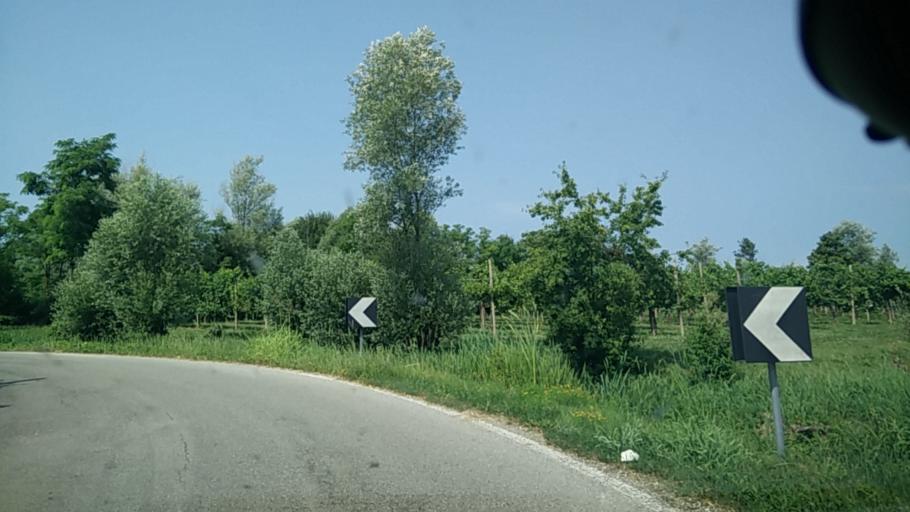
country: IT
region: Veneto
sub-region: Provincia di Treviso
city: Gaiarine
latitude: 45.8503
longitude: 12.4955
